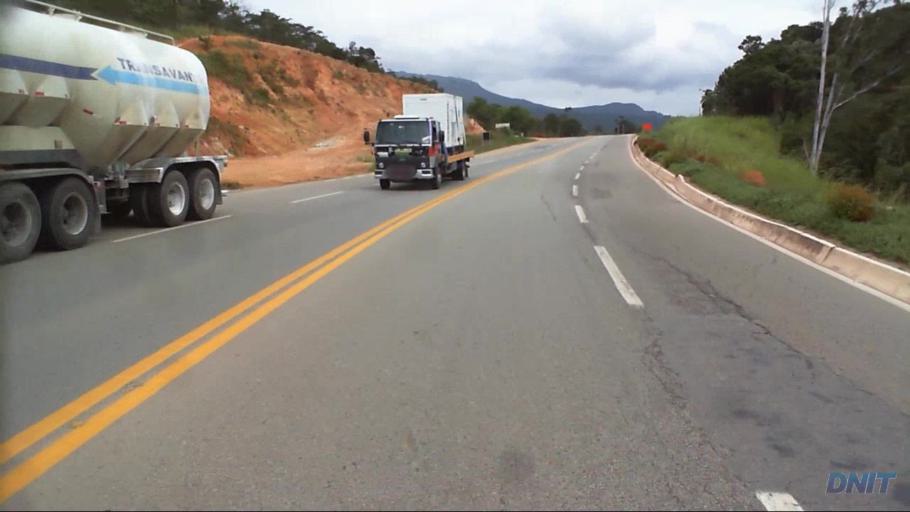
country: BR
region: Minas Gerais
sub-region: Caete
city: Caete
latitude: -19.7737
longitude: -43.6507
